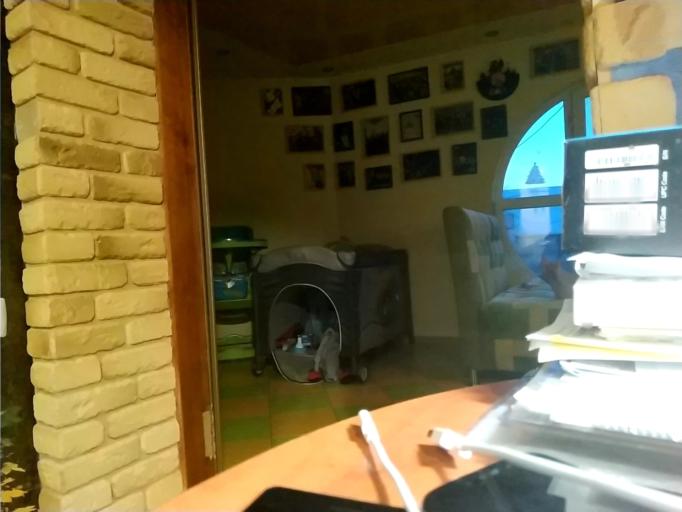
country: RU
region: Republic of Karelia
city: Belomorsk
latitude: 64.4285
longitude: 34.6779
